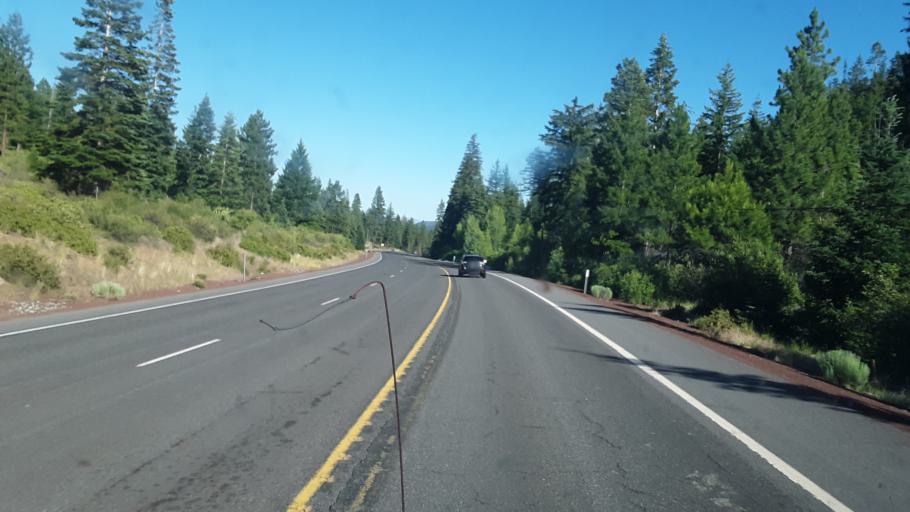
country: US
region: Oregon
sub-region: Klamath County
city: Klamath Falls
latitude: 42.3279
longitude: -121.9543
